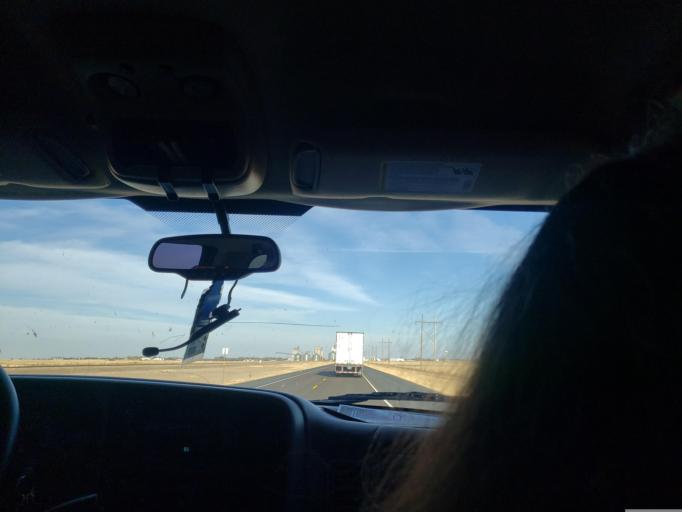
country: US
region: Oklahoma
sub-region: Texas County
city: Goodwell
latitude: 36.4883
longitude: -101.8073
